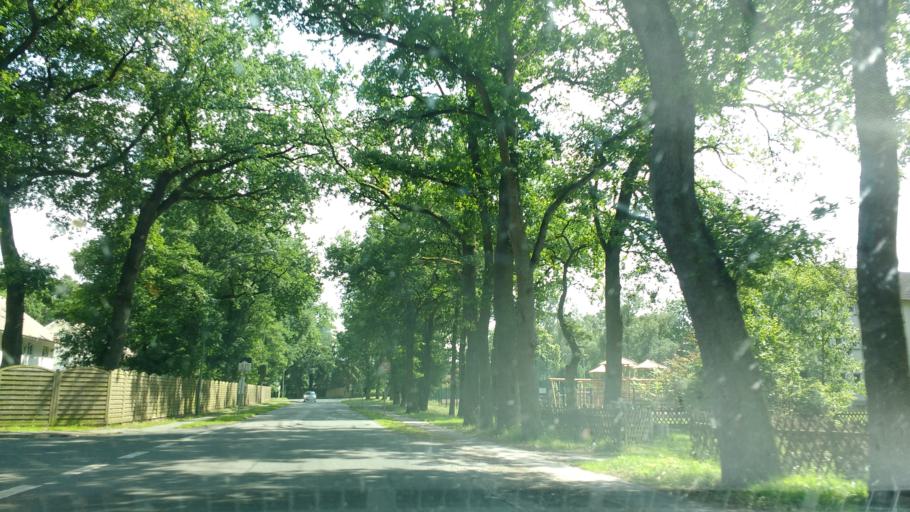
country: DE
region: North Rhine-Westphalia
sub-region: Regierungsbezirk Detmold
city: Paderborn
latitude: 51.7689
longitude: 8.7274
